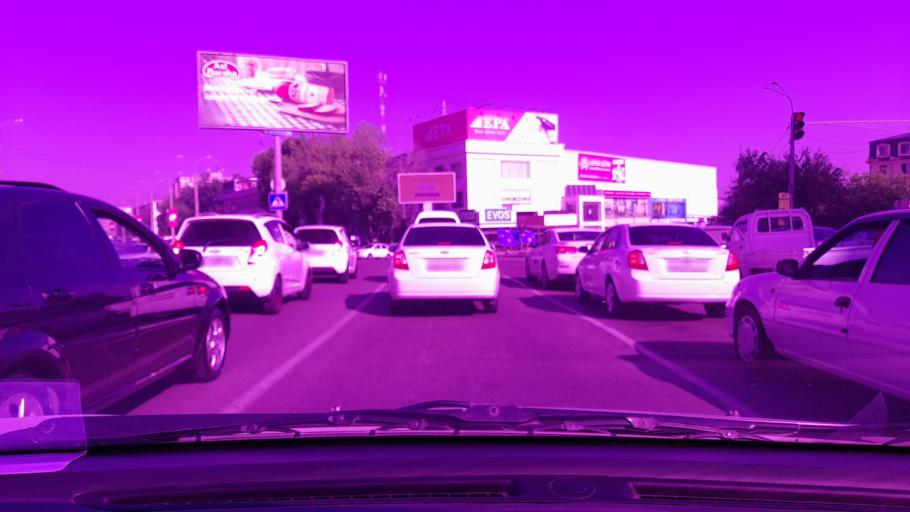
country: UZ
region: Toshkent
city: Salor
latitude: 41.3145
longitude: 69.3292
